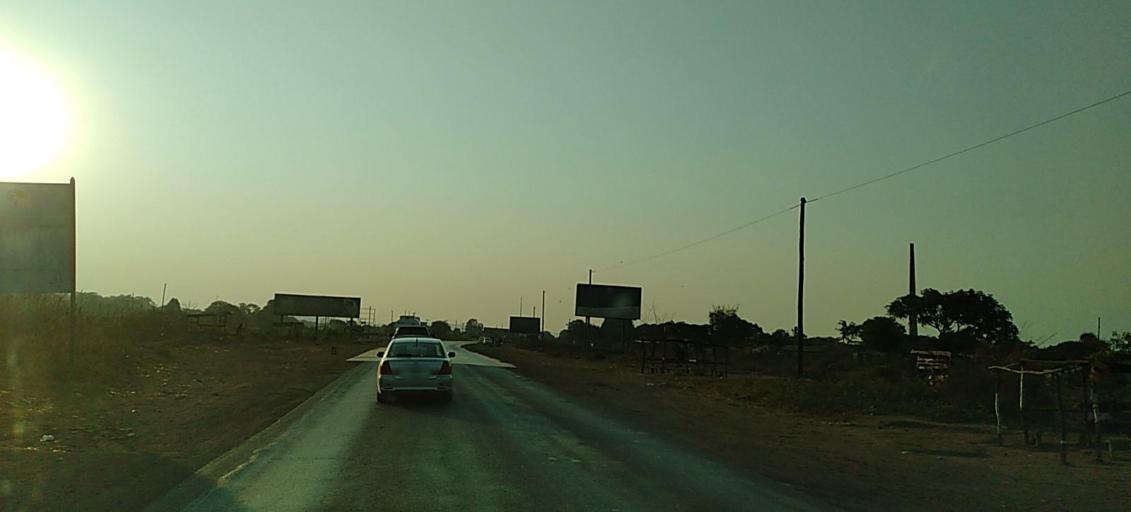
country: ZM
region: Copperbelt
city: Ndola
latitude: -13.0321
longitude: 28.6865
